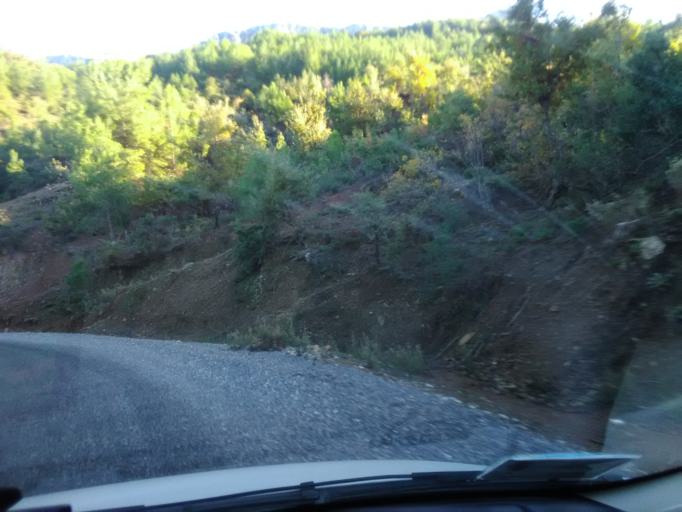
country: TR
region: Antalya
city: Gazipasa
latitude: 36.3053
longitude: 32.4015
